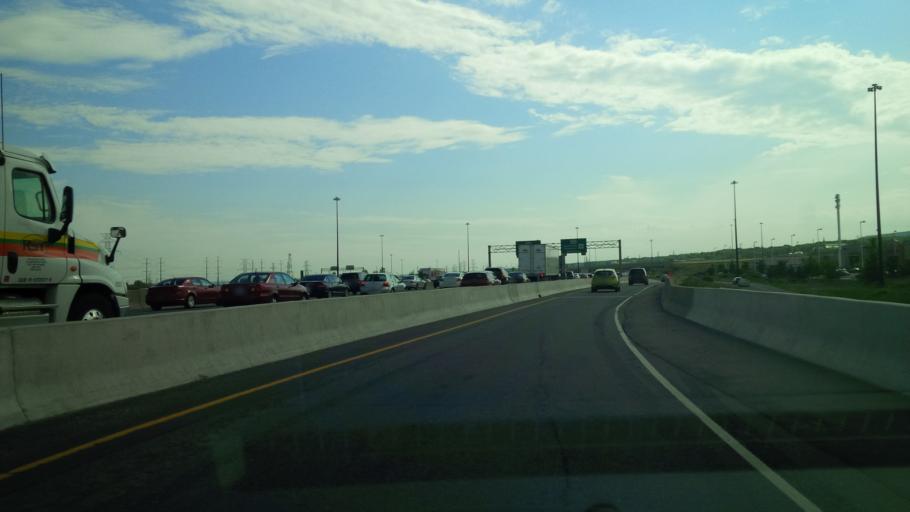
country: CA
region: Ontario
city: Burlington
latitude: 43.3422
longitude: -79.8220
